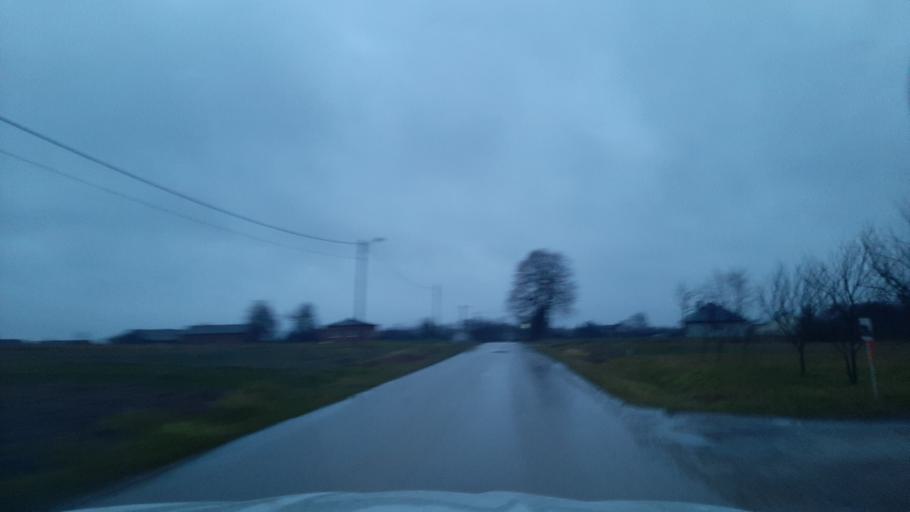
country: PL
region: Lublin Voivodeship
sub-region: Powiat lubelski
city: Jastkow
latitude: 51.3607
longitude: 22.4343
